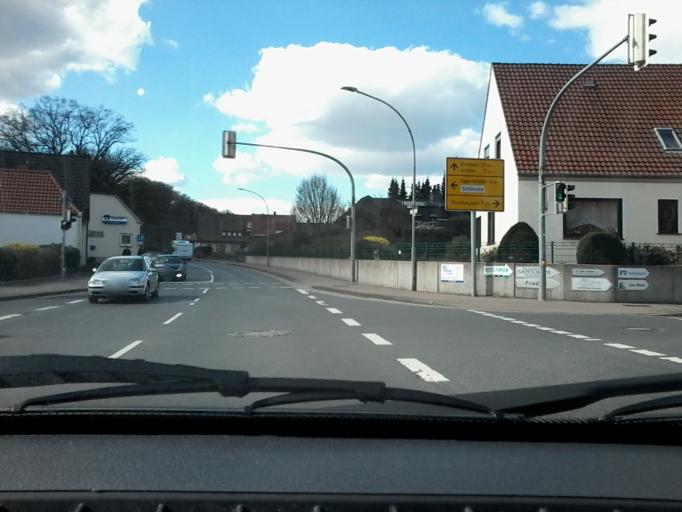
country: DE
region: Lower Saxony
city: Ahsen-Oetzen
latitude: 52.9952
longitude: 9.1164
